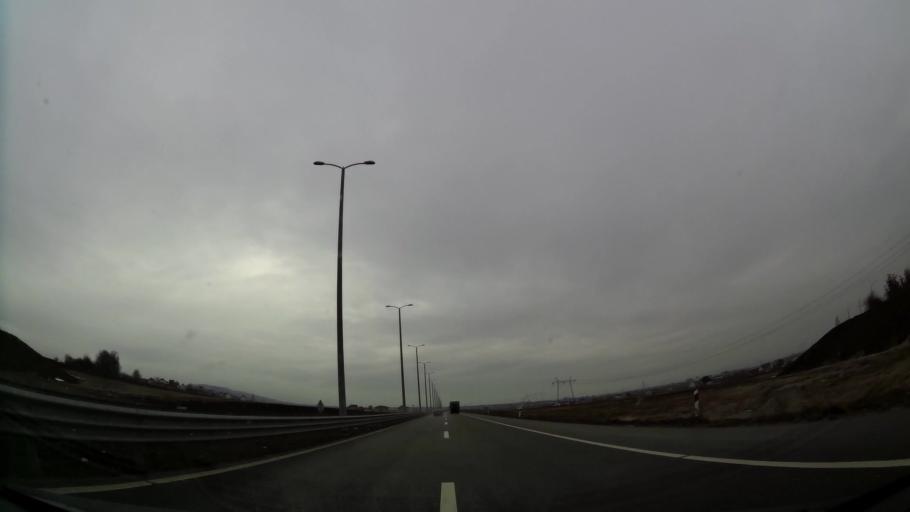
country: XK
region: Pristina
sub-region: Lipjan
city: Lipljan
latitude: 42.4971
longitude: 21.1872
